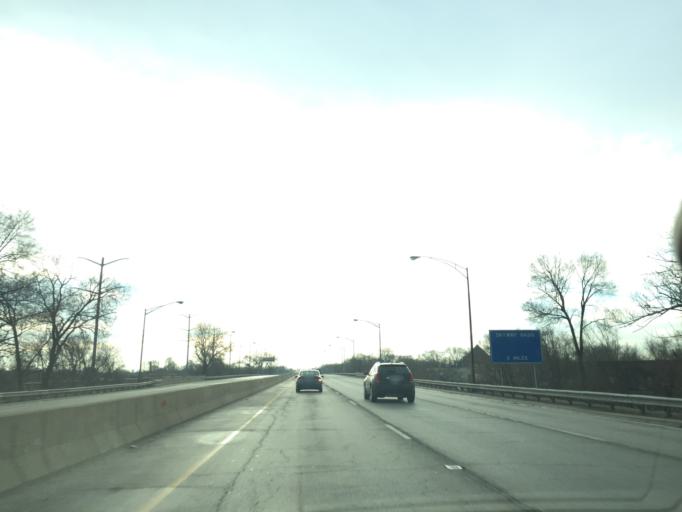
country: US
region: Illinois
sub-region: Cook County
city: Chicago
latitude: 41.7648
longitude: -87.6068
